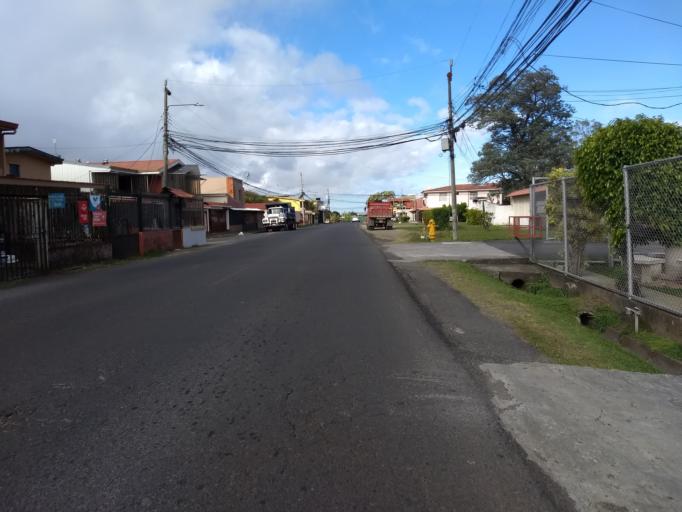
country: CR
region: San Jose
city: San Vicente de Moravia
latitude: 9.9668
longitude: -84.0555
